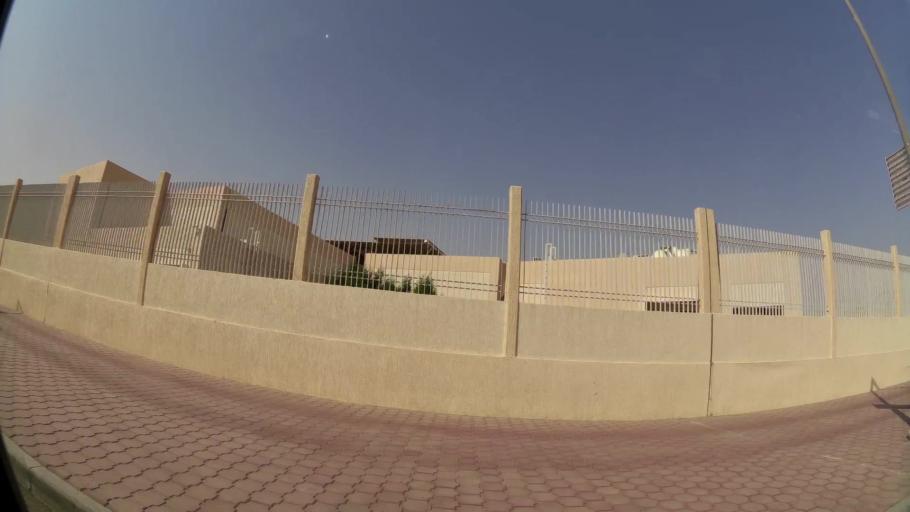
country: KW
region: Muhafazat al Jahra'
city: Al Jahra'
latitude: 29.3284
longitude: 47.7776
